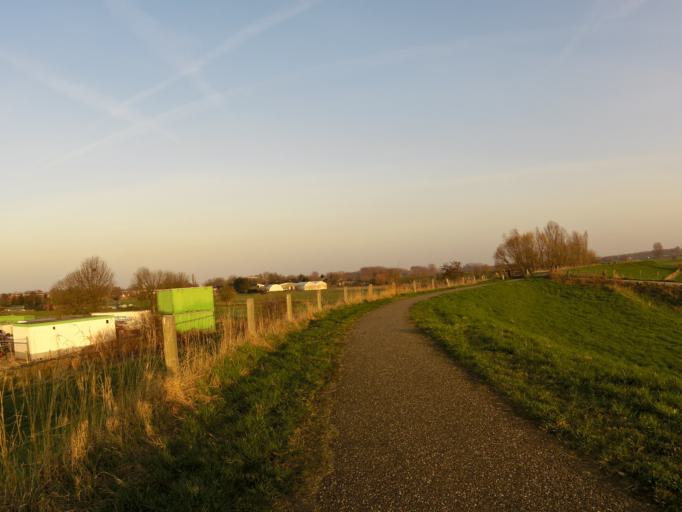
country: NL
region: Gelderland
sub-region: Gemeente Maasdriel
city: Hedel
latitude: 51.7417
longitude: 5.2500
